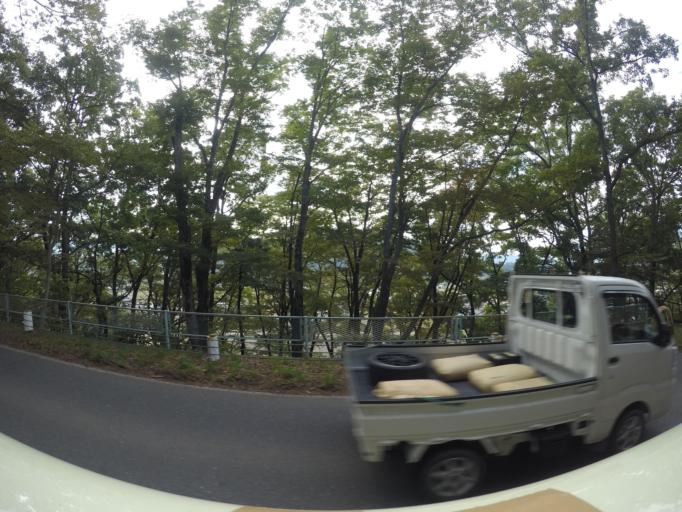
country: JP
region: Nagano
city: Ina
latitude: 35.8371
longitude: 138.0102
